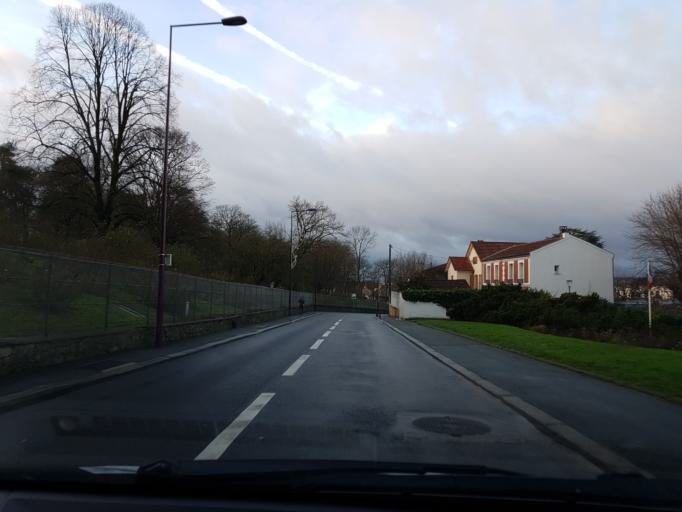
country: FR
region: Ile-de-France
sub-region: Departement du Val-de-Marne
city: L'Hay-les-Roses
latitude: 48.7771
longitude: 2.3325
